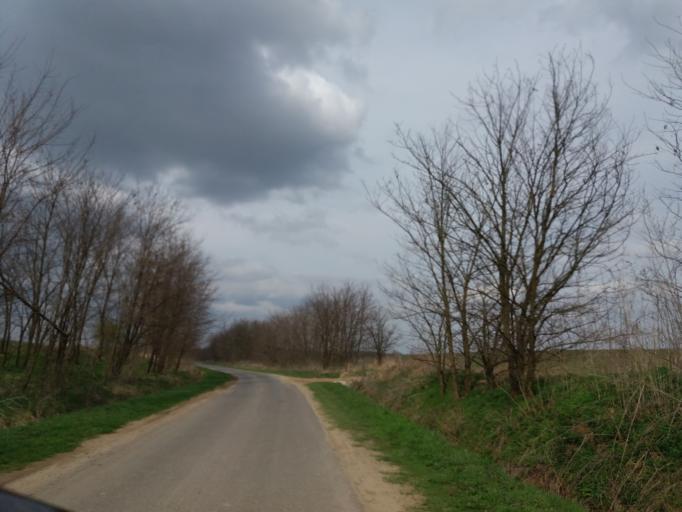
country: HU
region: Szabolcs-Szatmar-Bereg
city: Petnehaza
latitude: 48.0637
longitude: 22.0462
